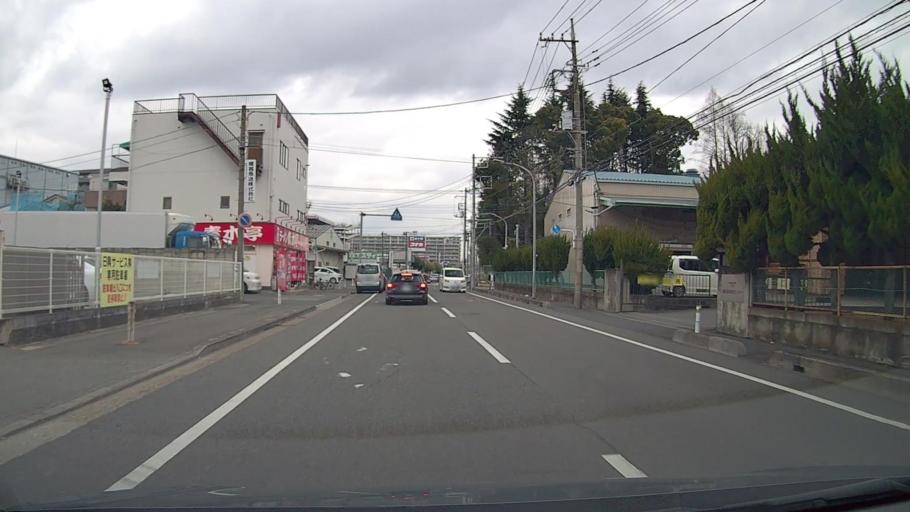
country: JP
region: Saitama
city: Shimotoda
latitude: 35.8231
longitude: 139.6547
